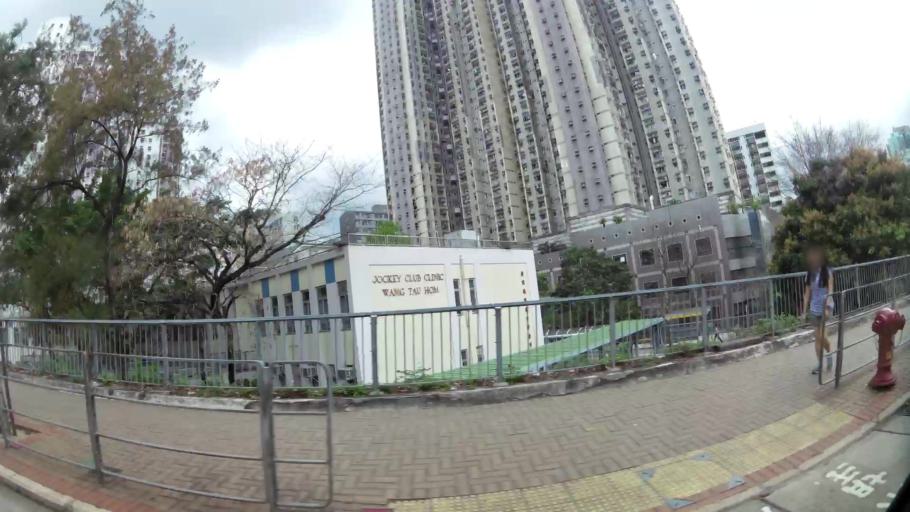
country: HK
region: Wong Tai Sin
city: Wong Tai Sin
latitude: 22.3387
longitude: 114.1853
